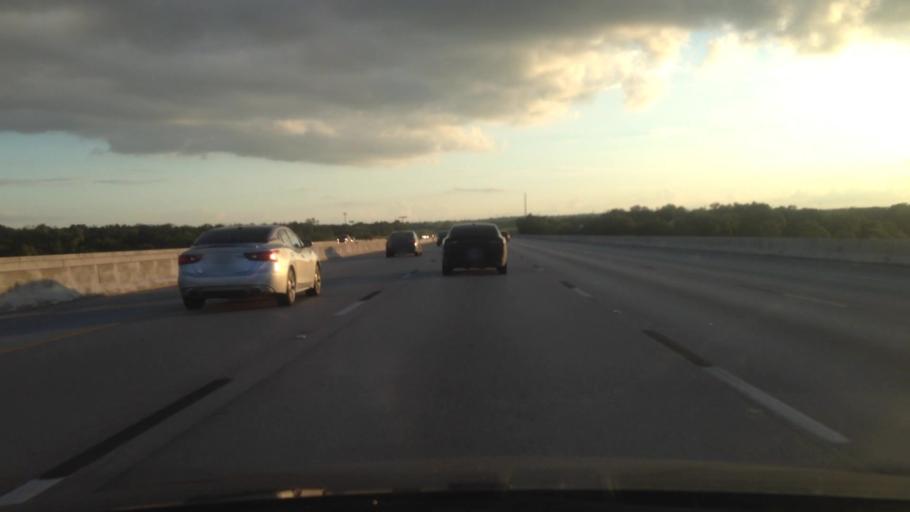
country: US
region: Texas
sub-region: Tarrant County
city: Lake Worth
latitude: 32.7922
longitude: -97.4557
